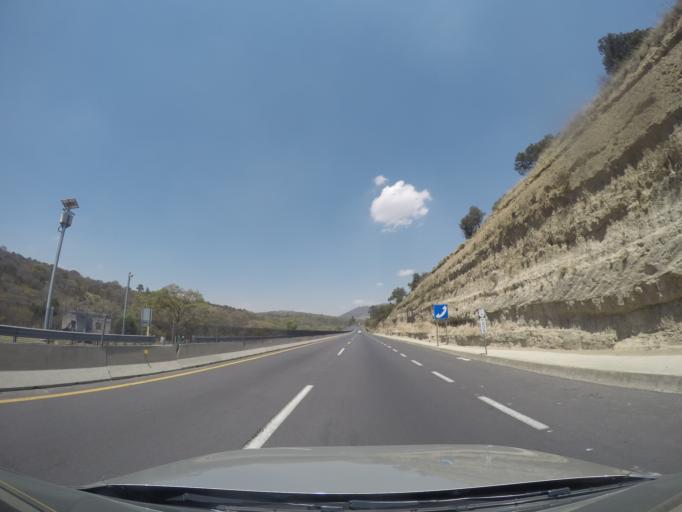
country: MX
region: Tlaxcala
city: Espanita
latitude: 19.4473
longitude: -98.4395
